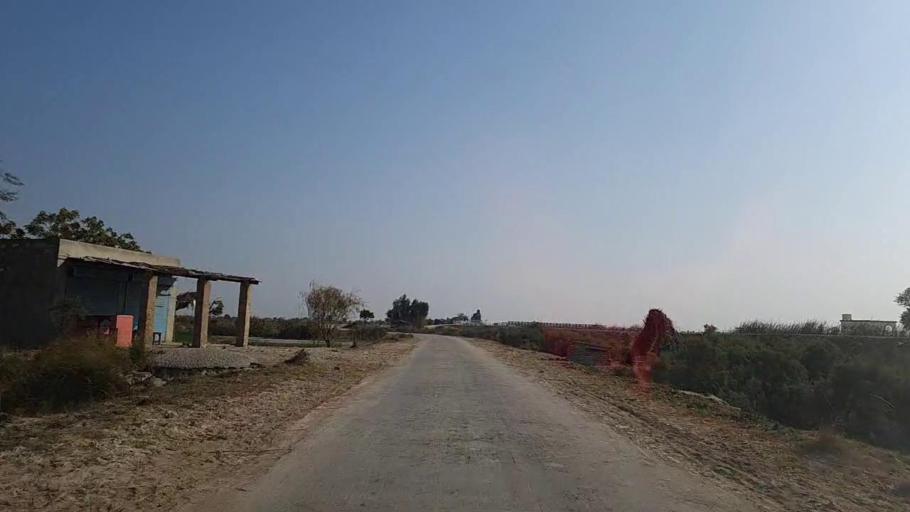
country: PK
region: Sindh
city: Sanghar
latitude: 25.9507
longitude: 69.0466
